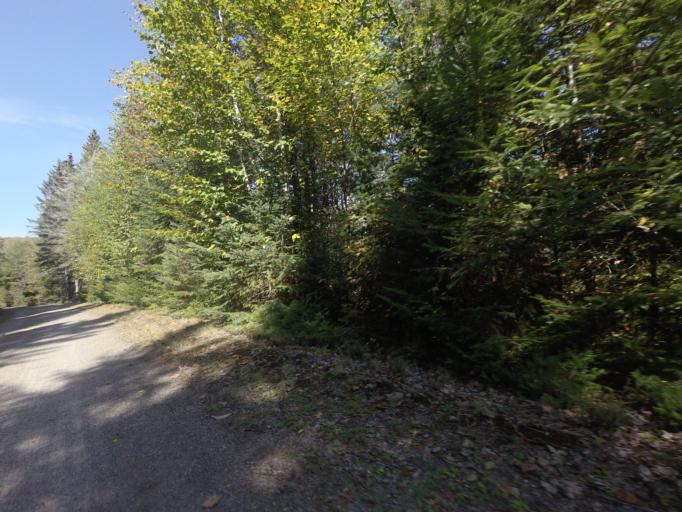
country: CA
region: Quebec
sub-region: Laurentides
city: Sainte-Agathe-des-Monts
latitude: 46.1033
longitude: -74.3643
